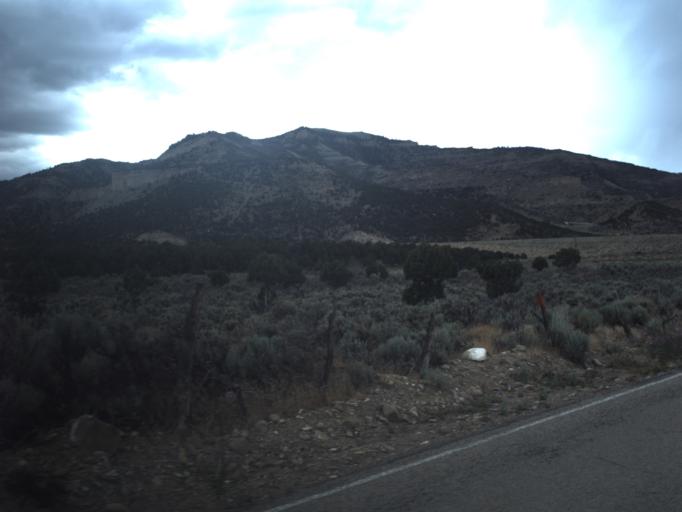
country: US
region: Utah
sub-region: Emery County
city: Huntington
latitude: 39.4842
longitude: -110.9920
